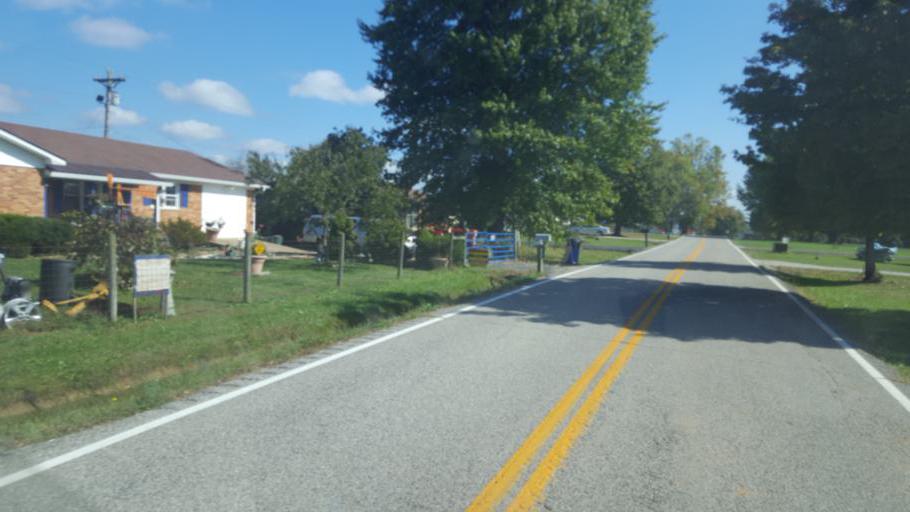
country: US
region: Ohio
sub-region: Adams County
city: Manchester
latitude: 38.5696
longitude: -83.6322
